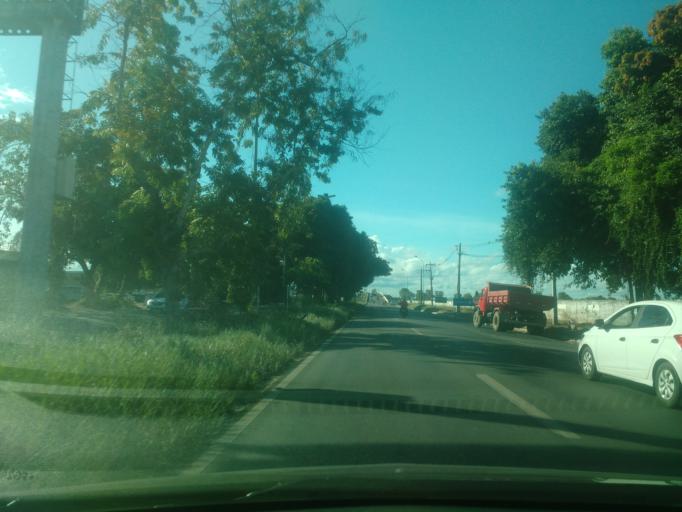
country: BR
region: Alagoas
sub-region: Satuba
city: Satuba
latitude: -9.5181
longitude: -35.8032
